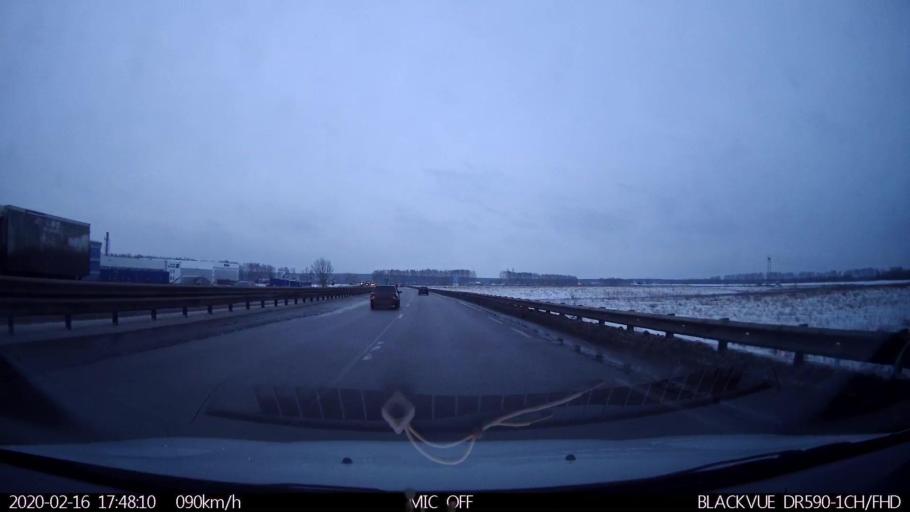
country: RU
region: Nizjnij Novgorod
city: Afonino
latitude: 56.2149
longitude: 44.0791
